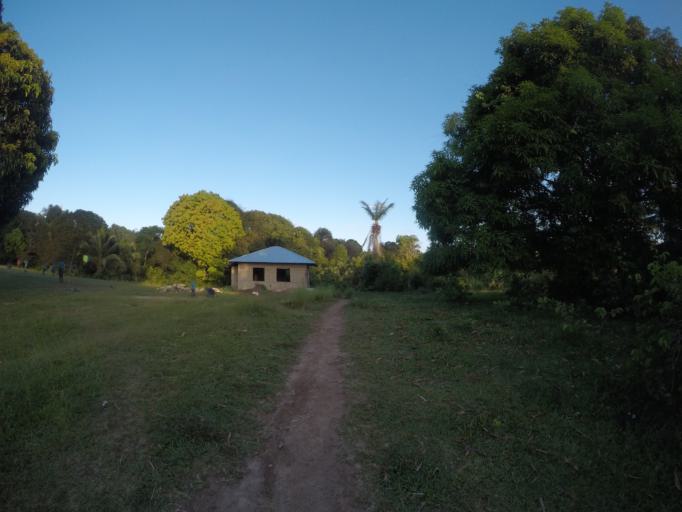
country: TZ
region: Pemba South
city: Mtambile
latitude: -5.3786
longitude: 39.7063
